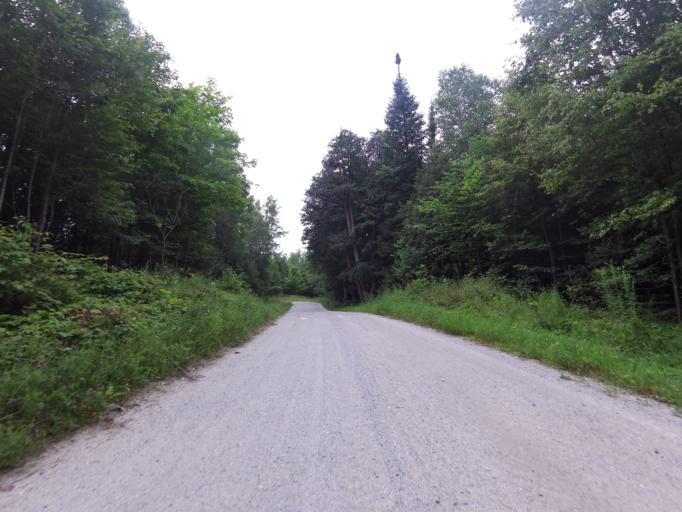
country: CA
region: Ontario
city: Perth
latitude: 44.8388
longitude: -76.5945
